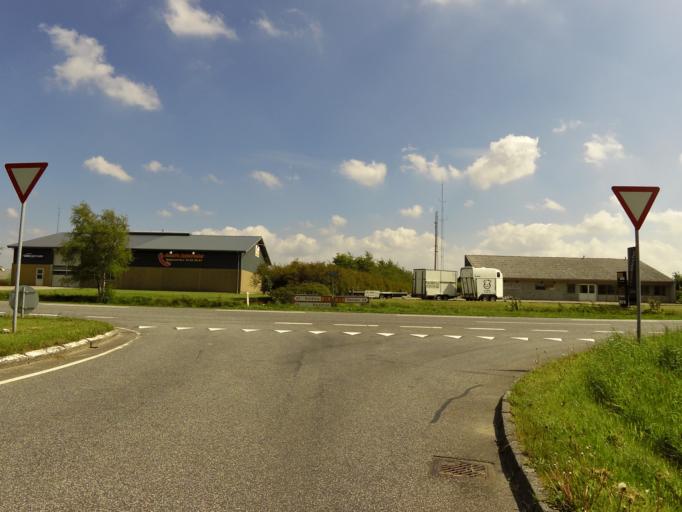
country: DK
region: South Denmark
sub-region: Tonder Kommune
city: Toftlund
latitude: 55.1932
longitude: 9.0767
